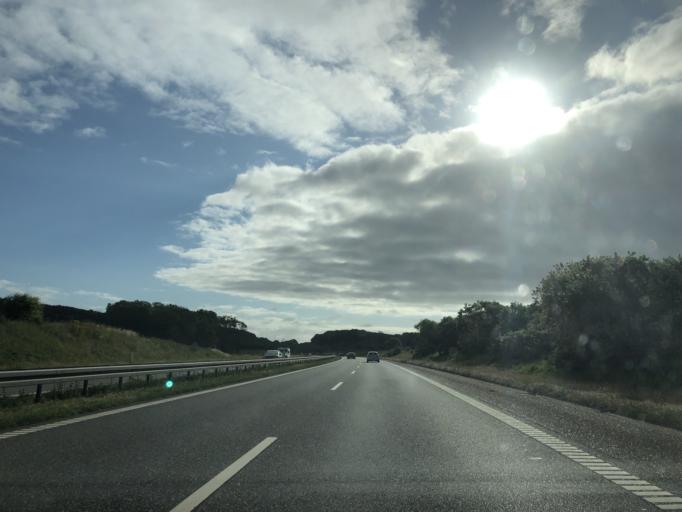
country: DK
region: Central Jutland
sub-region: Skanderborg Kommune
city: Skovby
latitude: 56.1427
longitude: 9.9542
